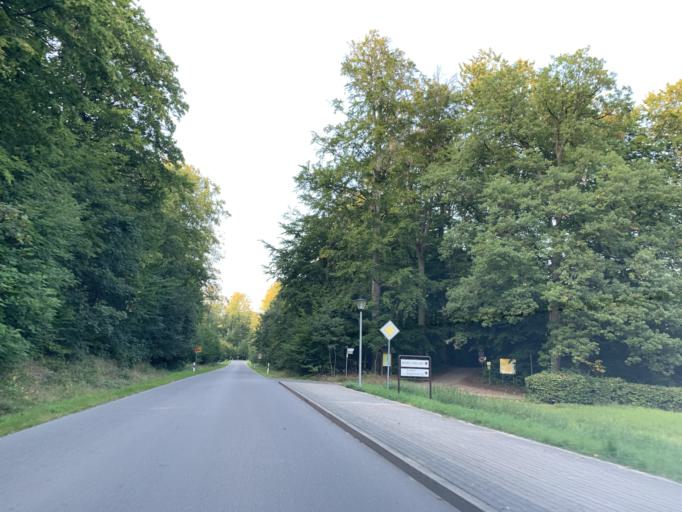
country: DE
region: Mecklenburg-Vorpommern
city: Loitz
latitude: 53.3458
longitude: 13.4300
